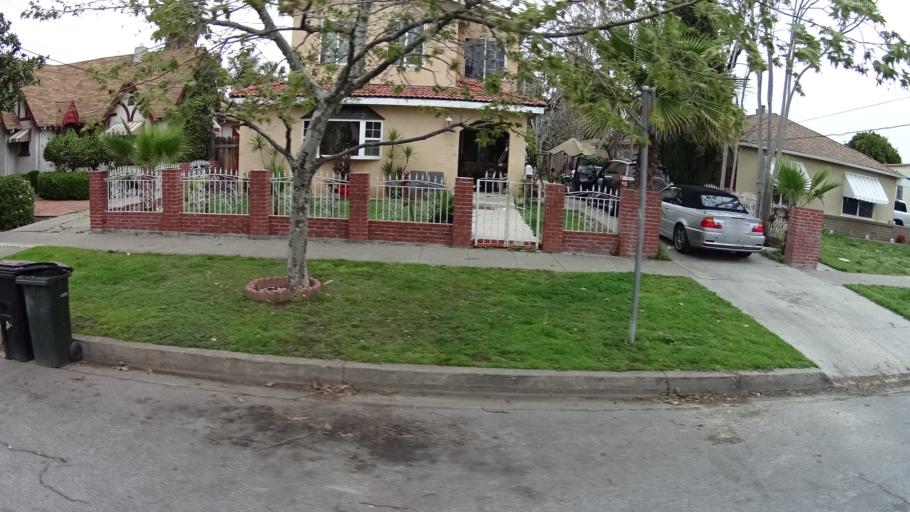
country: US
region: California
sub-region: Santa Clara County
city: San Jose
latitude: 37.3512
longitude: -121.8990
